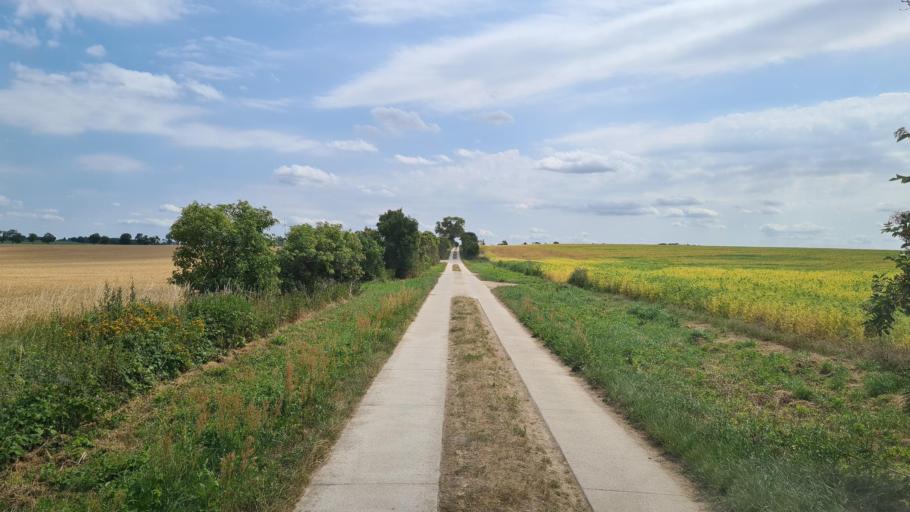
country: DE
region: Brandenburg
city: Juterbog
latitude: 51.9460
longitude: 13.1040
